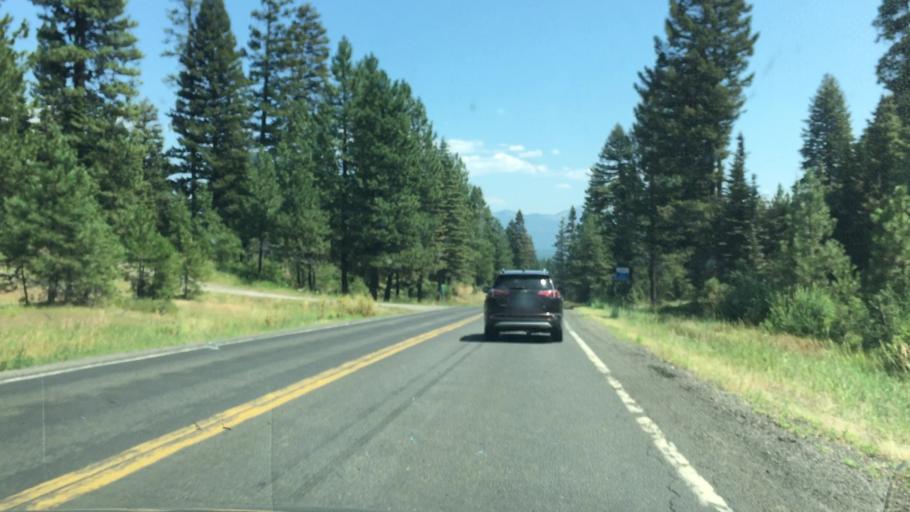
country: US
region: Idaho
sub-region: Valley County
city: McCall
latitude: 44.9288
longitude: -116.1511
